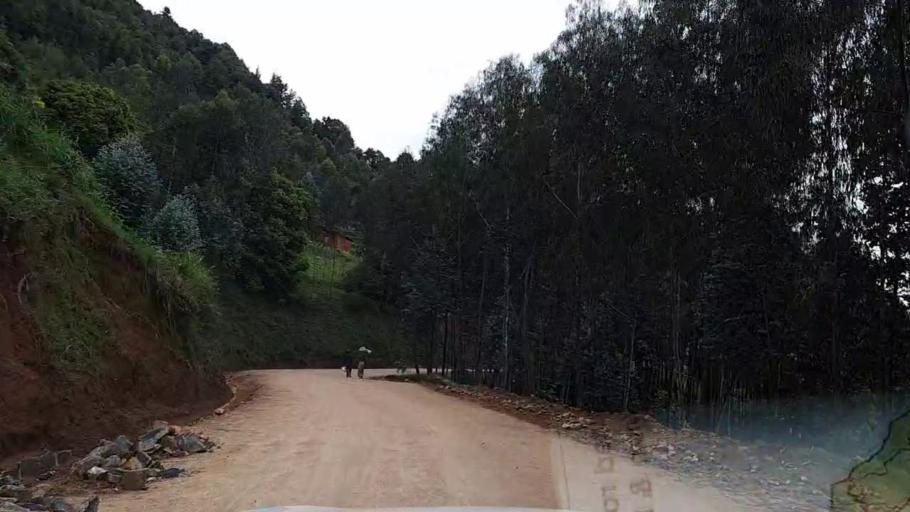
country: RW
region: Southern Province
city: Nzega
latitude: -2.4043
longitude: 29.4548
